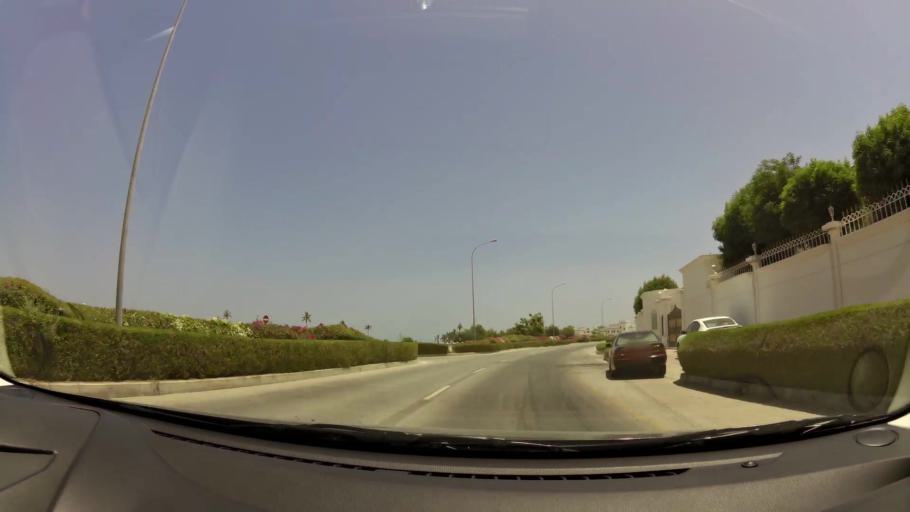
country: OM
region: Muhafazat Masqat
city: Bawshar
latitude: 23.6121
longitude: 58.4569
